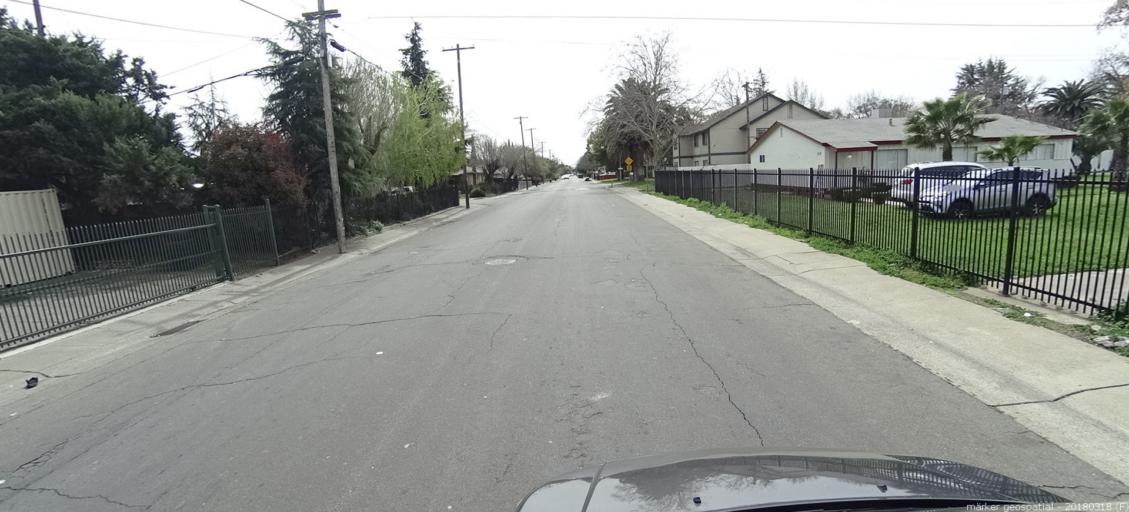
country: US
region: California
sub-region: Sacramento County
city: Parkway
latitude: 38.5242
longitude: -121.4476
